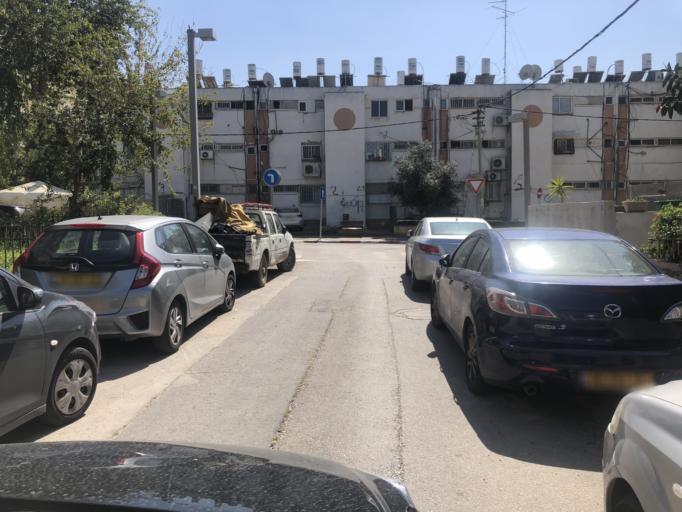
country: IL
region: Tel Aviv
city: Holon
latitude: 32.0021
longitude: 34.7624
